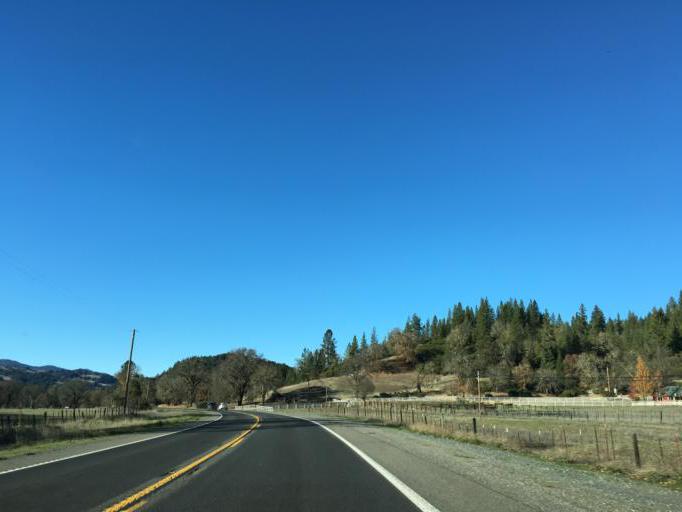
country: US
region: California
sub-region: Mendocino County
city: Laytonville
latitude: 39.7399
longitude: -123.5149
